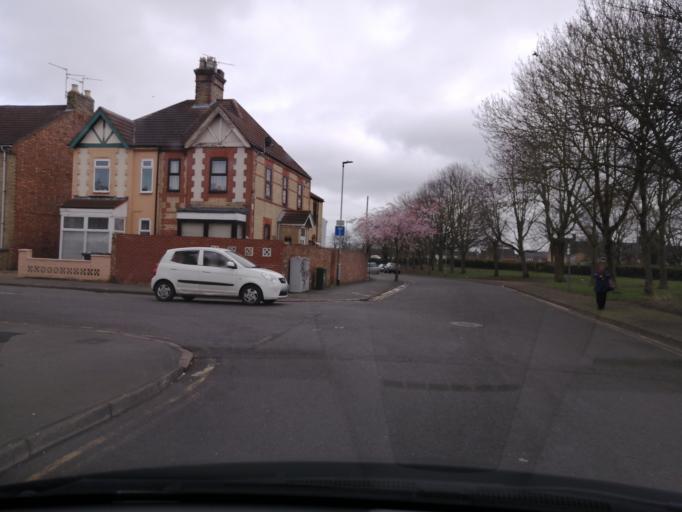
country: GB
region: England
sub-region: Peterborough
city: Peterborough
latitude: 52.5774
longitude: -0.2323
